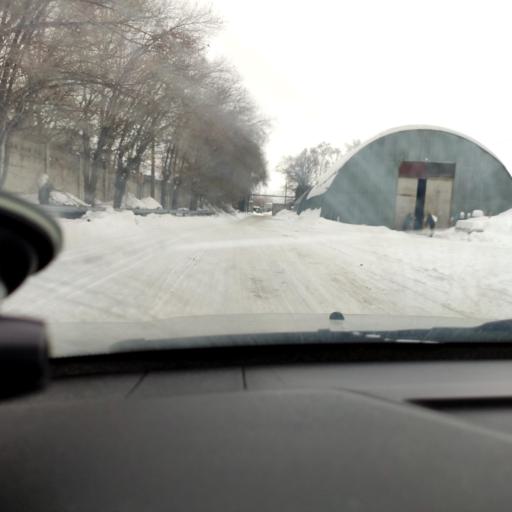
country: RU
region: Samara
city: Samara
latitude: 53.1944
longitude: 50.2695
